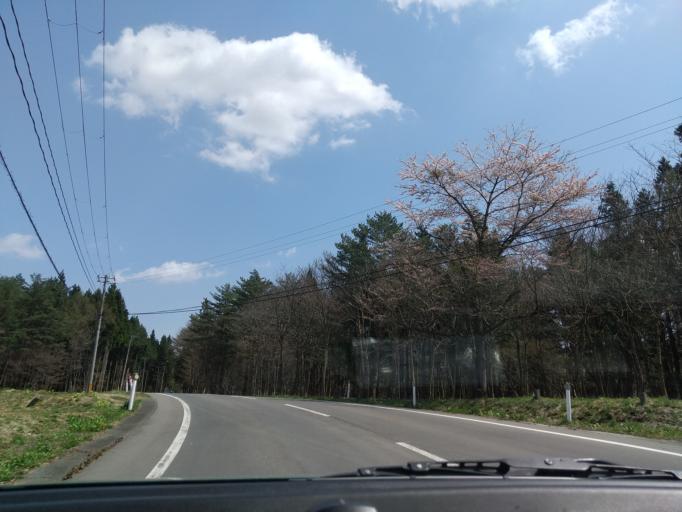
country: JP
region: Iwate
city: Kitakami
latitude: 39.2488
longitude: 140.9845
